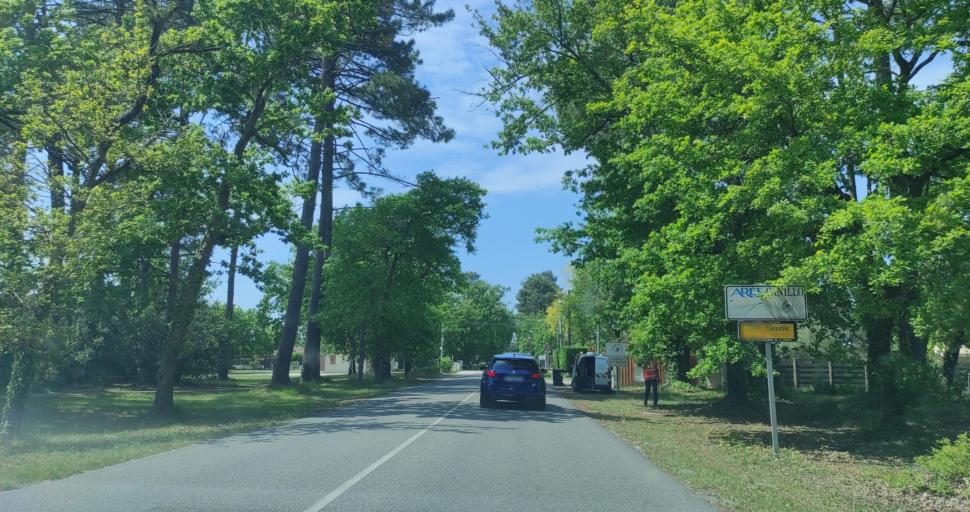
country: FR
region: Aquitaine
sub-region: Departement de la Gironde
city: Ares
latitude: 44.7598
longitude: -1.1240
